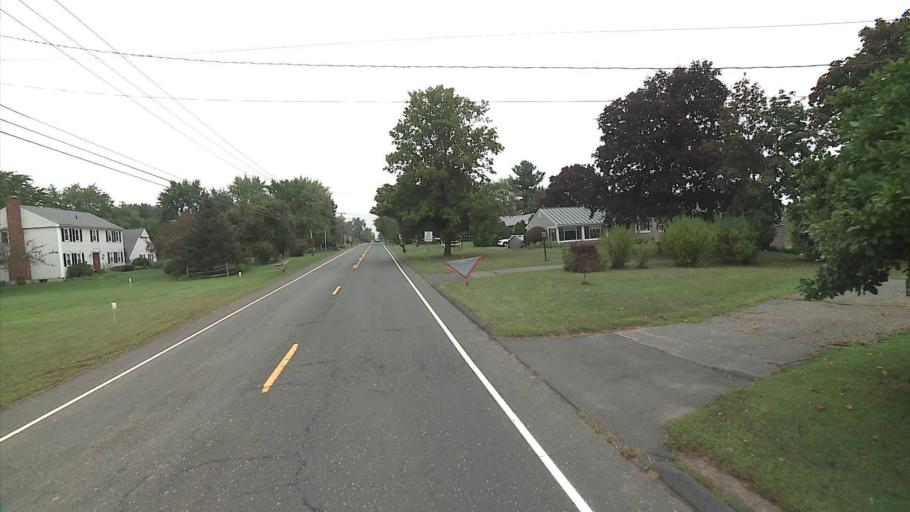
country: US
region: Connecticut
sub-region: Hartford County
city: Suffield Depot
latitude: 42.0207
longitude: -72.6396
